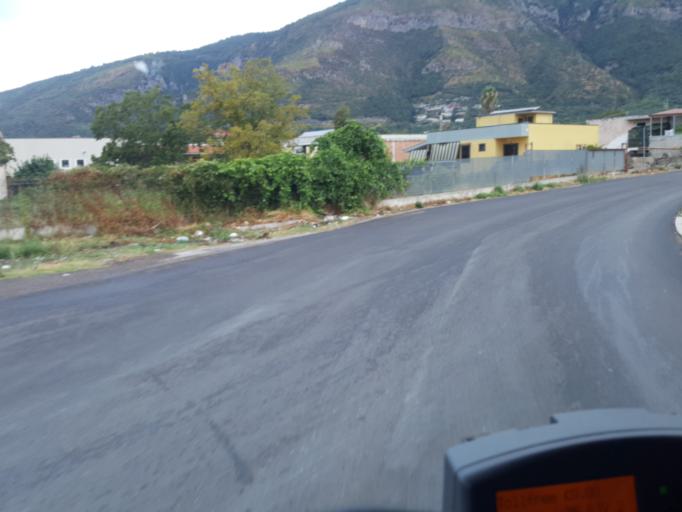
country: IT
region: Campania
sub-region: Provincia di Napoli
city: Striano
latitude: 40.8230
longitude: 14.5980
